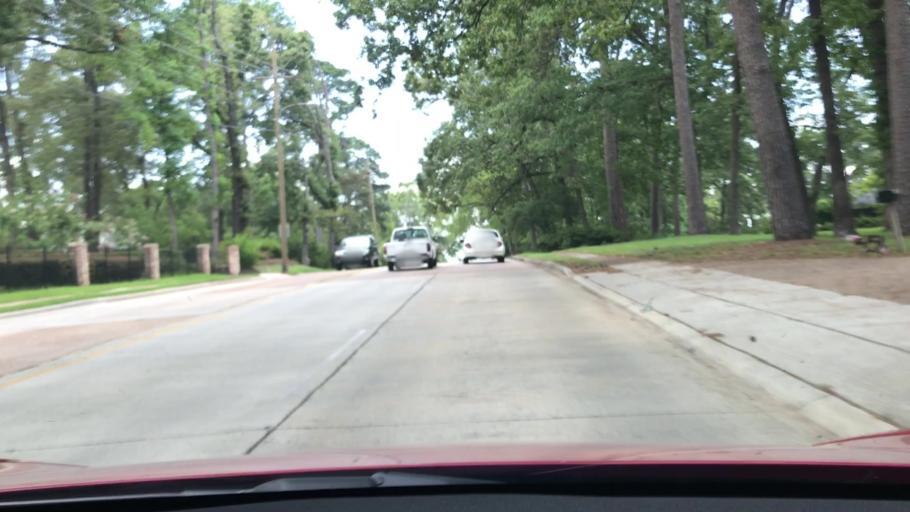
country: US
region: Louisiana
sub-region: Bossier Parish
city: Bossier City
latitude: 32.4547
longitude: -93.7396
